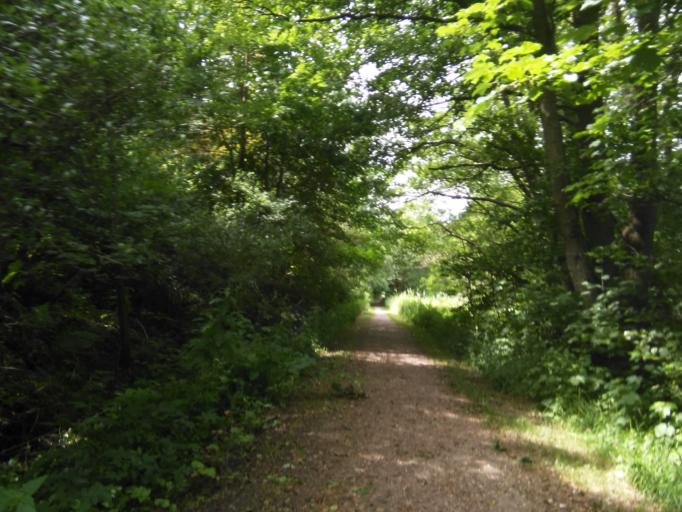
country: DK
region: Central Jutland
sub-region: Horsens Kommune
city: Horsens
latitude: 55.8753
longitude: 9.8566
